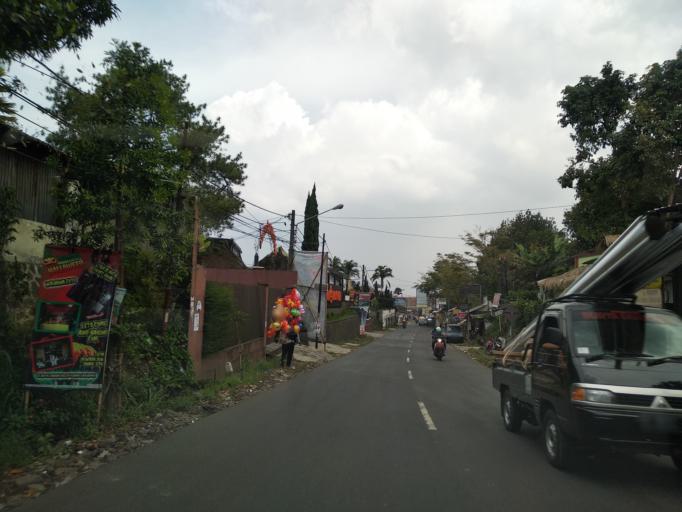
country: ID
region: West Java
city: Lembang
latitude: -6.8203
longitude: 107.6108
